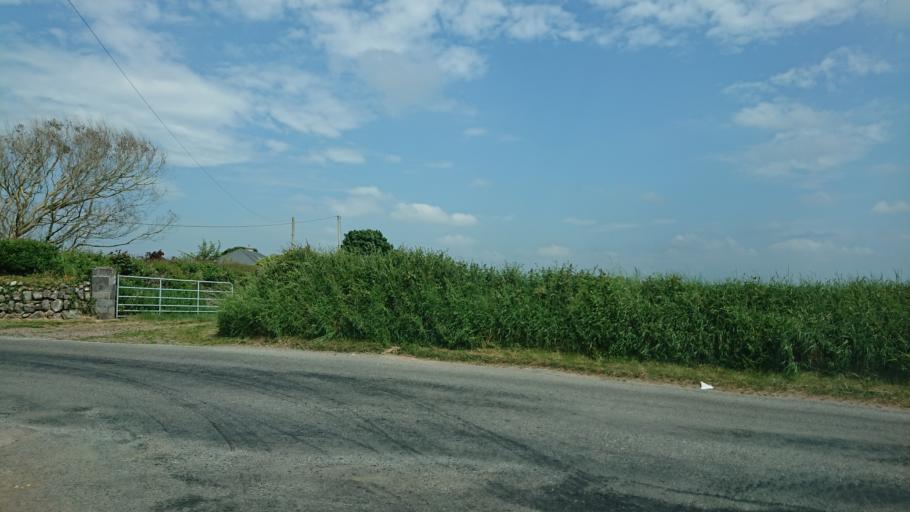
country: IE
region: Munster
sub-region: Waterford
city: Dunmore East
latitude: 52.2306
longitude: -7.0042
